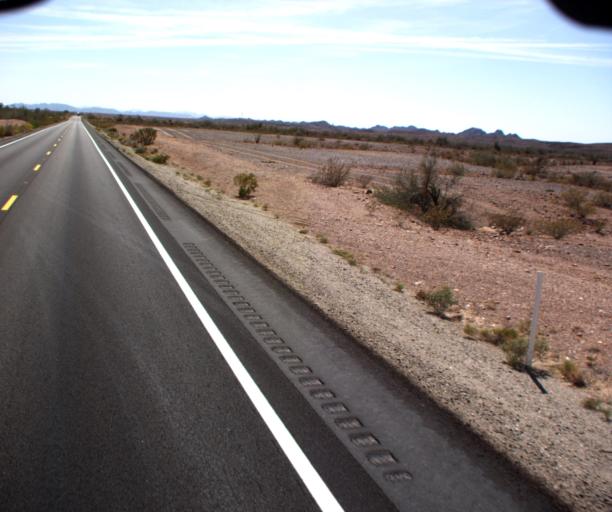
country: US
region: Arizona
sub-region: Yuma County
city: Wellton
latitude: 33.0625
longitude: -114.2930
